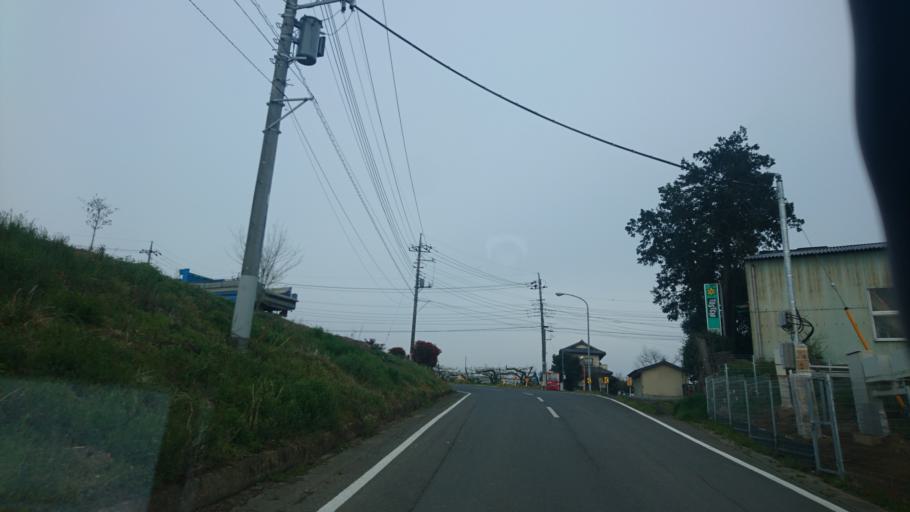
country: JP
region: Ibaraki
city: Shimodate
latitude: 36.2187
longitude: 139.9674
